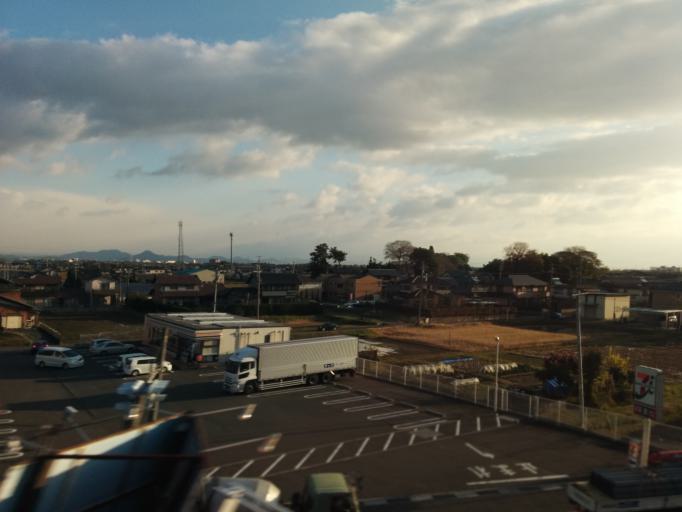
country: JP
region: Gifu
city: Ogaki
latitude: 35.3275
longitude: 136.6721
